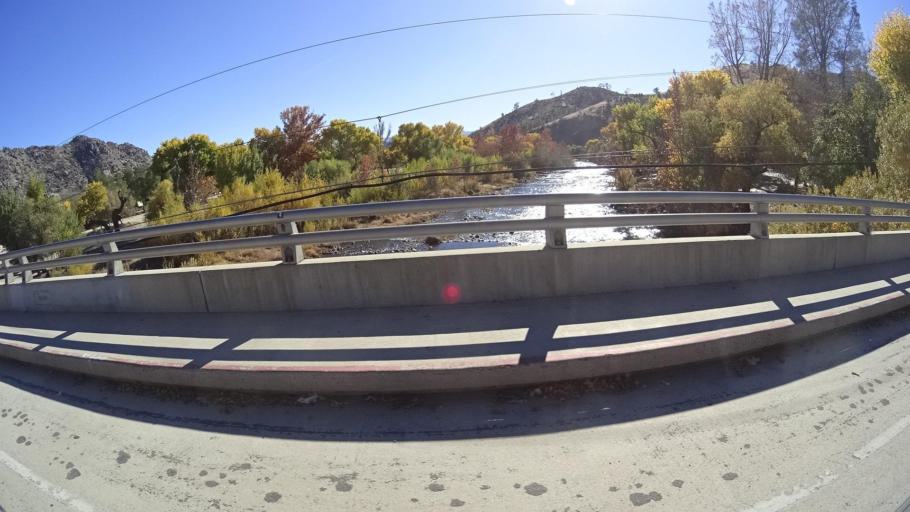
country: US
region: California
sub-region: Kern County
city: Kernville
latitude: 35.7552
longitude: -118.4229
